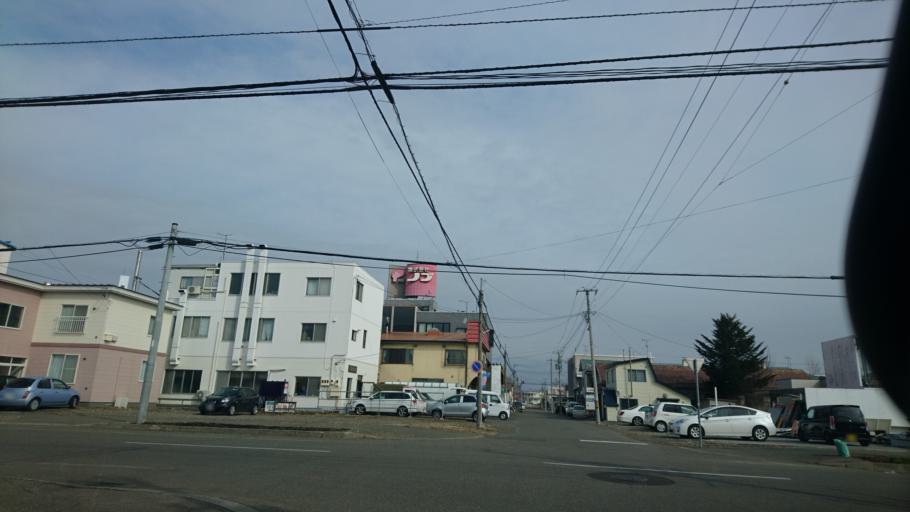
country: JP
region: Hokkaido
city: Obihiro
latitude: 42.9273
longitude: 143.2055
